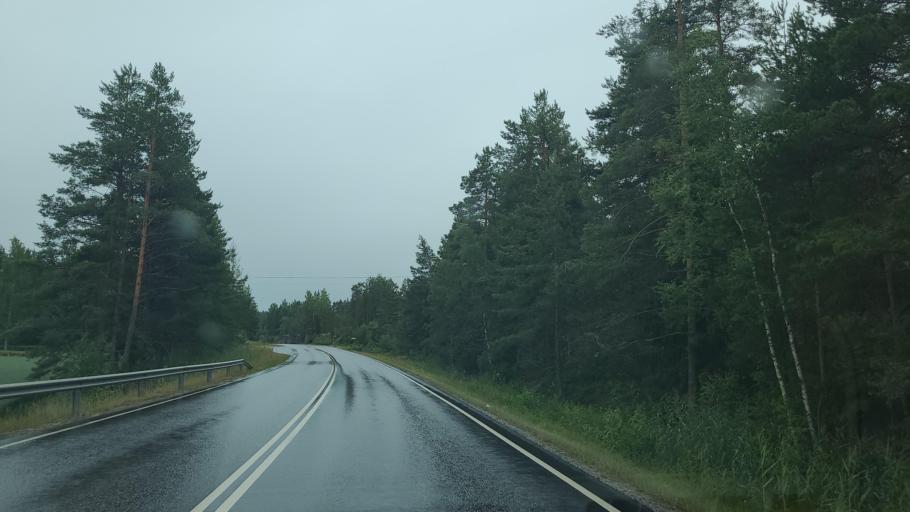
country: FI
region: Varsinais-Suomi
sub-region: Turku
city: Sauvo
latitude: 60.2789
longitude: 22.6685
